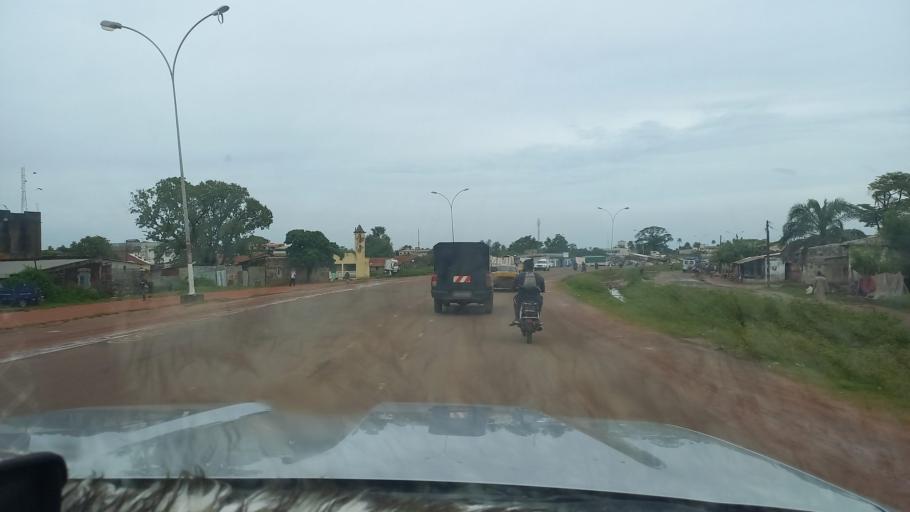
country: SN
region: Ziguinchor
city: Ziguinchor
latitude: 12.5732
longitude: -16.2717
